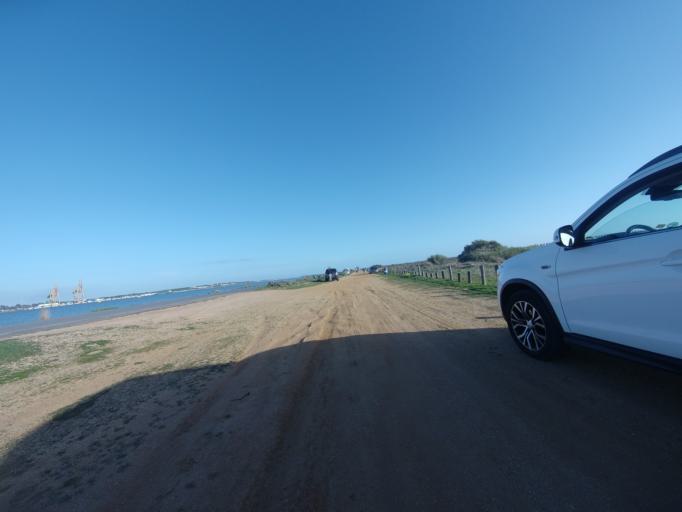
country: ES
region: Andalusia
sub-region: Provincia de Huelva
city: Punta Umbria
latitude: 37.1481
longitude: -6.8933
